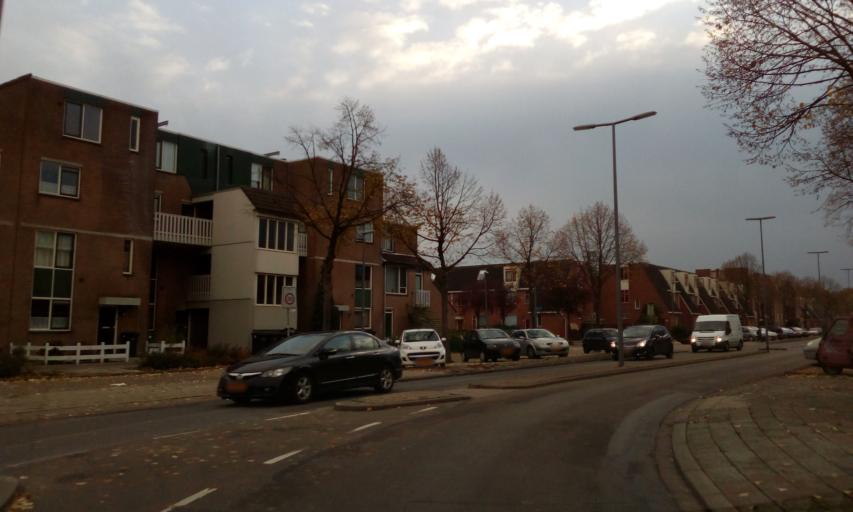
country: NL
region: South Holland
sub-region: Gemeente Capelle aan den IJssel
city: Capelle aan den IJssel
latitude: 51.9632
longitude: 4.5708
